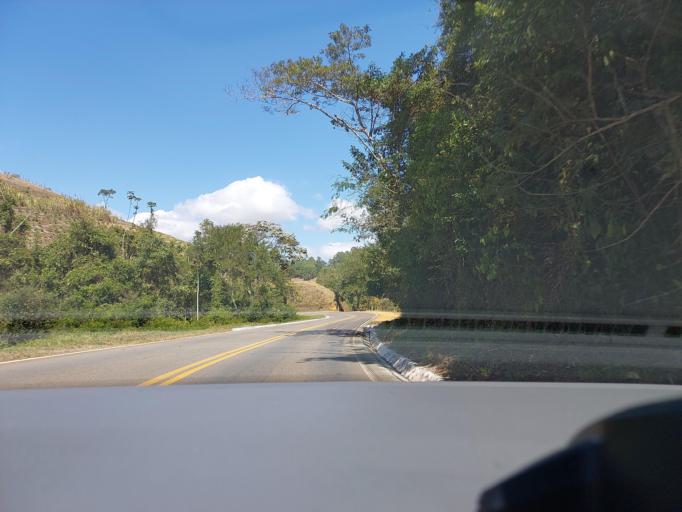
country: BR
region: Minas Gerais
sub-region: Mirai
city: Mirai
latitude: -21.0222
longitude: -42.5412
